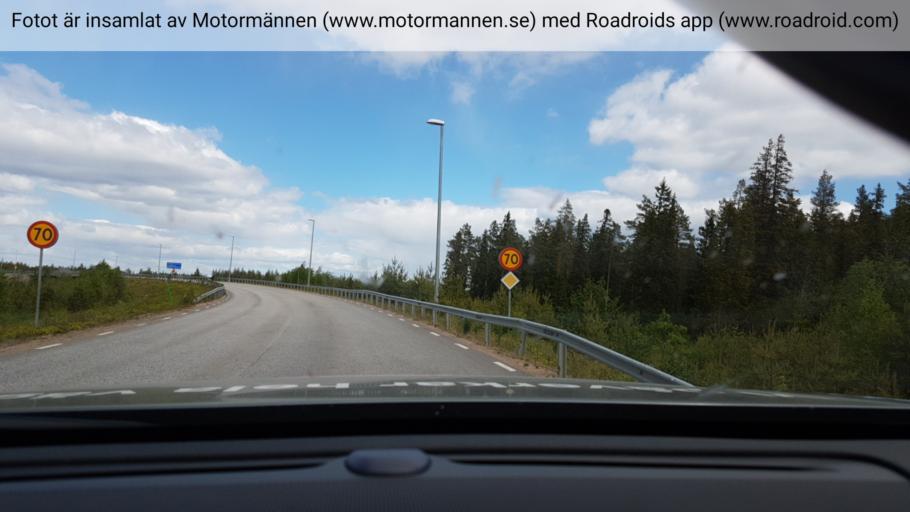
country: SE
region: Vaesterbotten
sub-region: Nordmalings Kommun
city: Nordmaling
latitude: 63.5803
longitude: 19.5335
